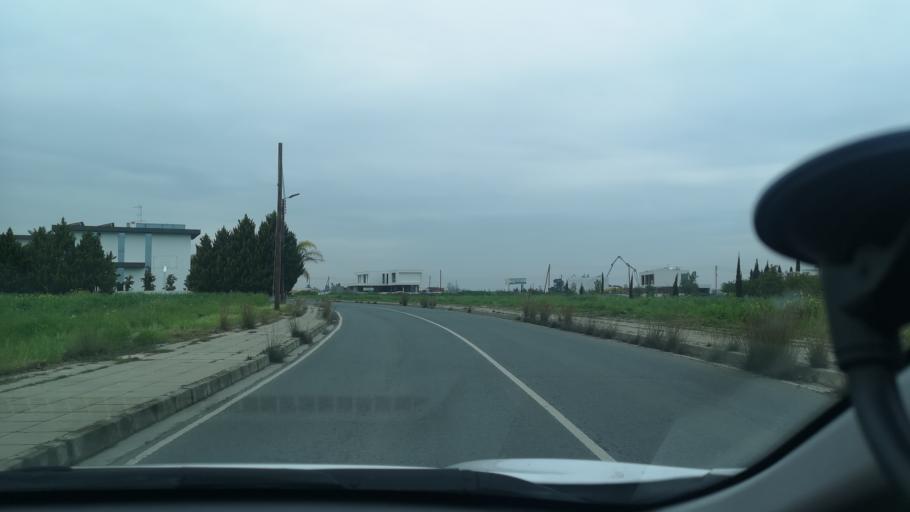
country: CY
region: Lefkosia
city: Tseri
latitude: 35.1083
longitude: 33.3525
